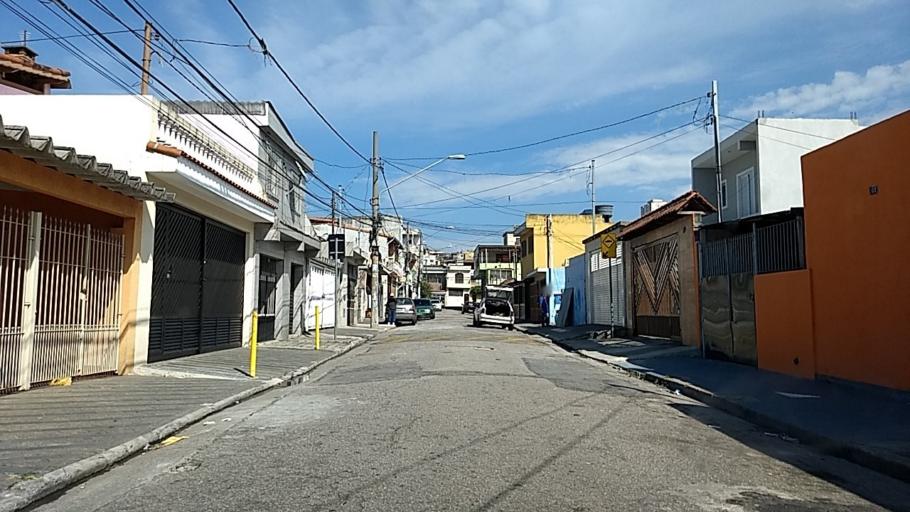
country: BR
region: Sao Paulo
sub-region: Guarulhos
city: Guarulhos
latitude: -23.4926
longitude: -46.5763
